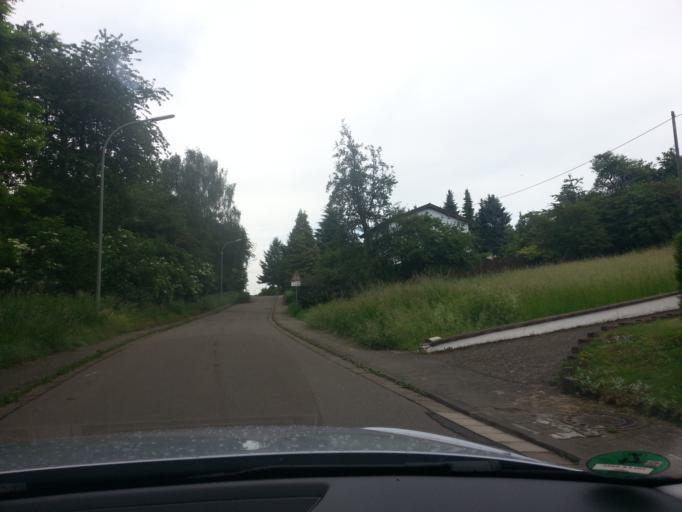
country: DE
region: Saarland
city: Sankt Wendel
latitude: 49.4964
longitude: 7.1668
